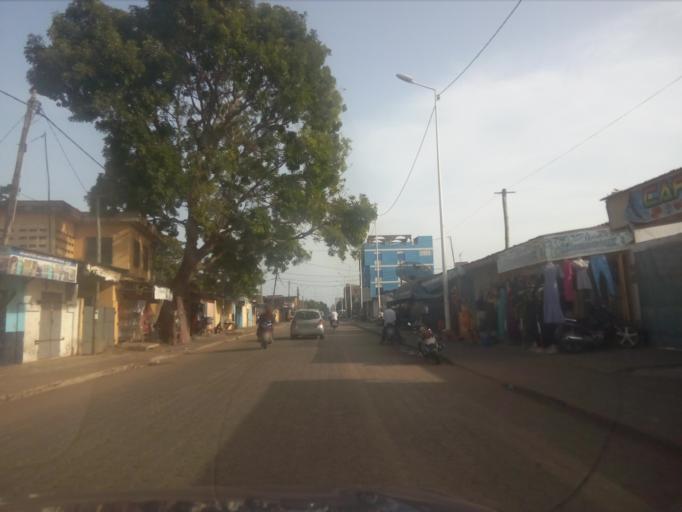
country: TG
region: Maritime
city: Lome
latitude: 6.1437
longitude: 1.2288
